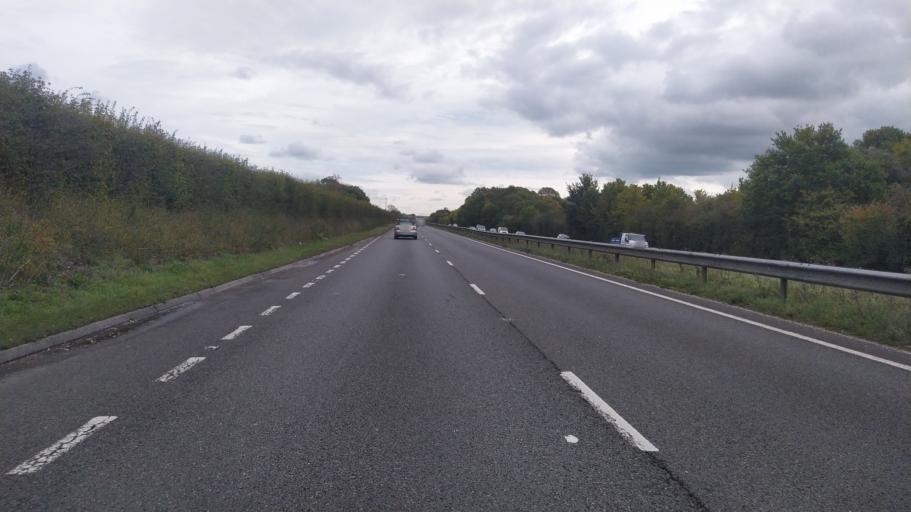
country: GB
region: England
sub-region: Poole
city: Poole
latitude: 50.7384
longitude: -2.0082
